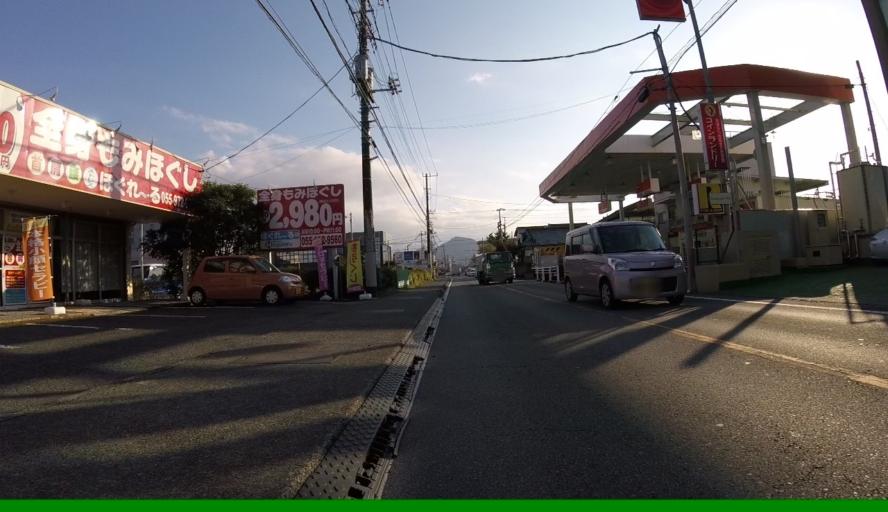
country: JP
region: Shizuoka
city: Mishima
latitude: 35.0984
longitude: 138.9045
